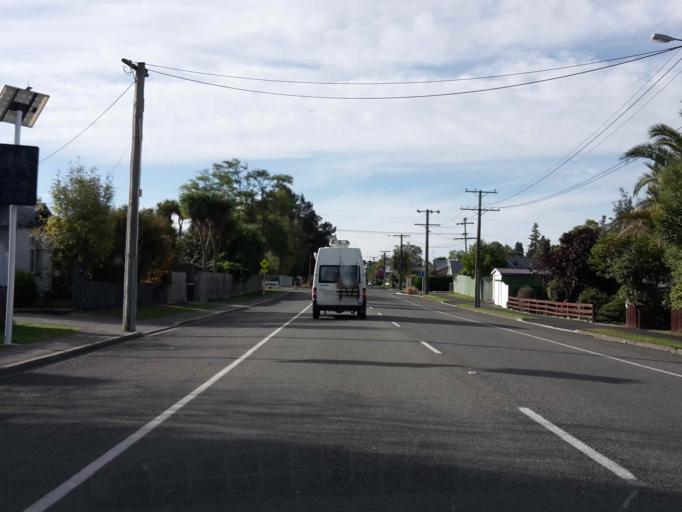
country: NZ
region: Canterbury
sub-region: Timaru District
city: Pleasant Point
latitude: -44.0988
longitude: 171.2390
